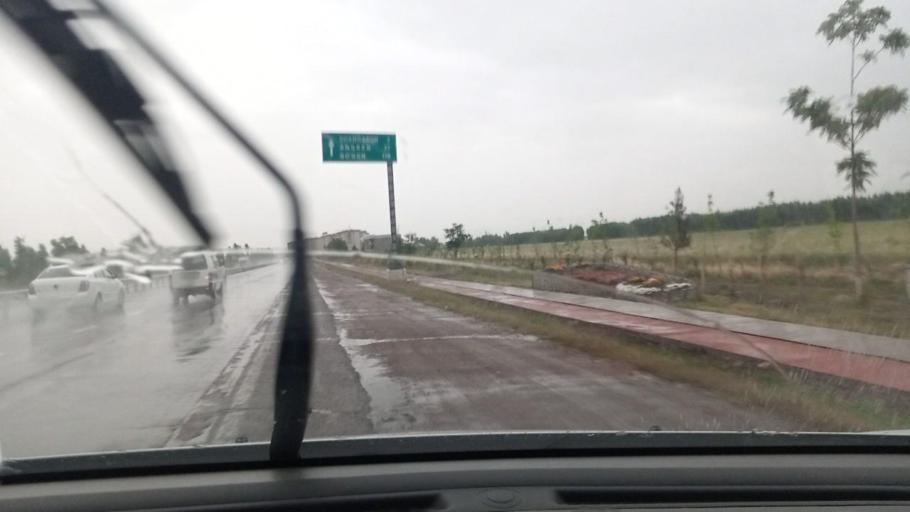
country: UZ
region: Toshkent
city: Ohangaron
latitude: 40.9180
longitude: 69.6017
